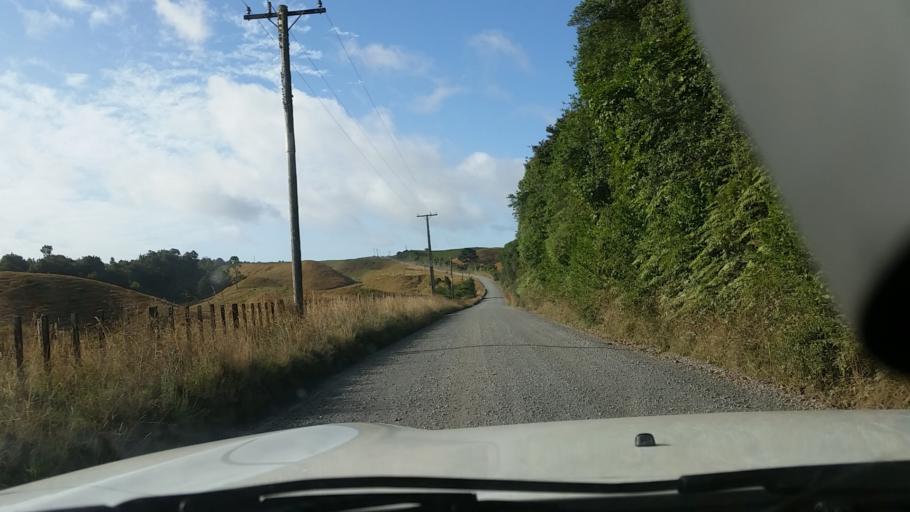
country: NZ
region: Bay of Plenty
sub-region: Rotorua District
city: Rotorua
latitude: -38.1424
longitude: 176.0814
